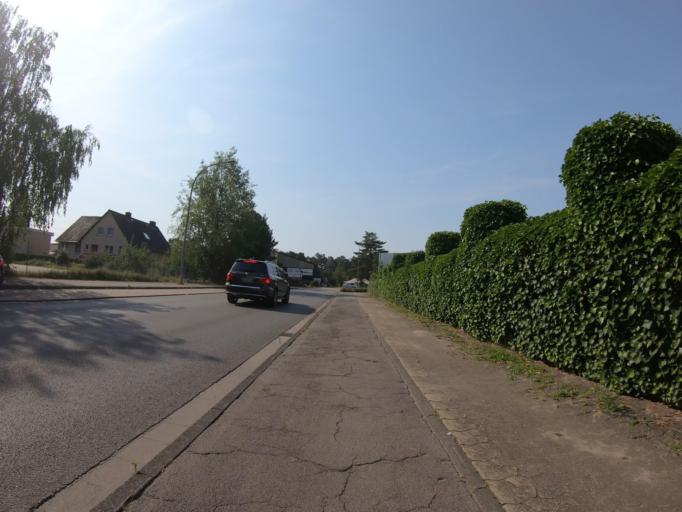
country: DE
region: Lower Saxony
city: Gifhorn
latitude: 52.4651
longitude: 10.5303
